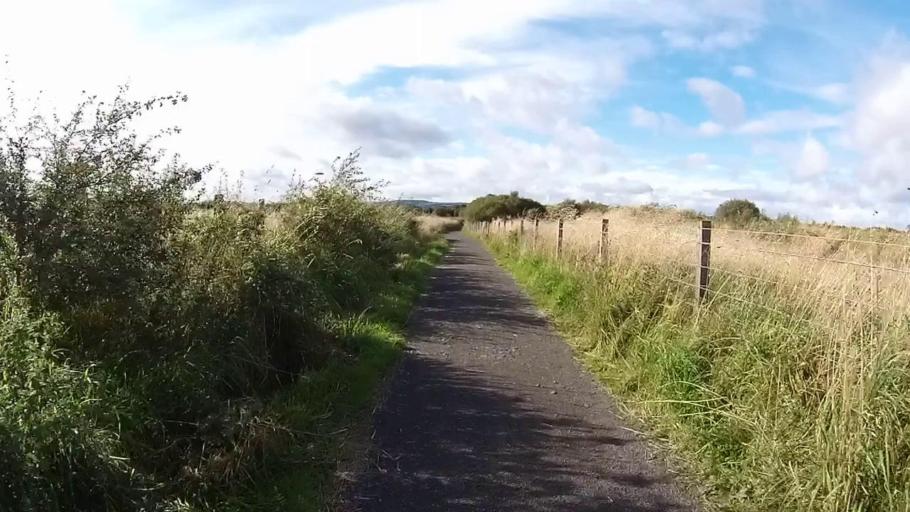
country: GB
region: Scotland
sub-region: Perth and Kinross
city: Kinross
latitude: 56.1936
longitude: -3.4159
